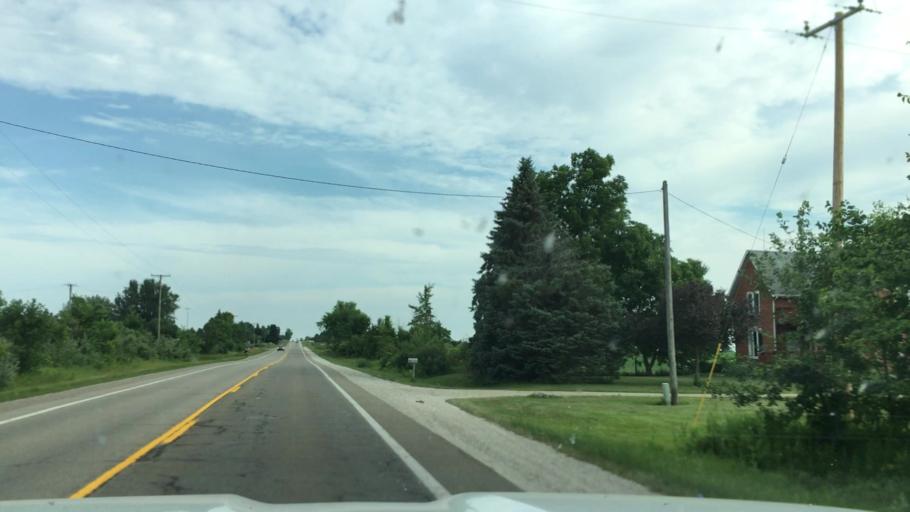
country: US
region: Michigan
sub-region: Sanilac County
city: Brown City
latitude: 43.1991
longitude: -83.0770
